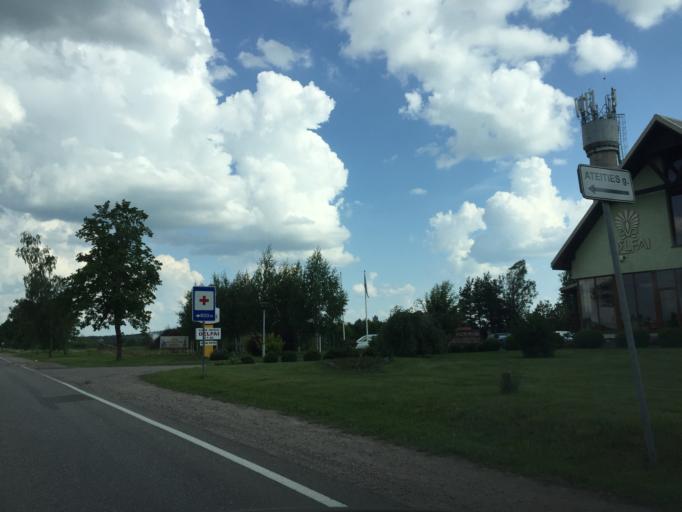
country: LT
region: Klaipedos apskritis
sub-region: Klaipeda
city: Palanga
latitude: 55.9003
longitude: 21.1367
